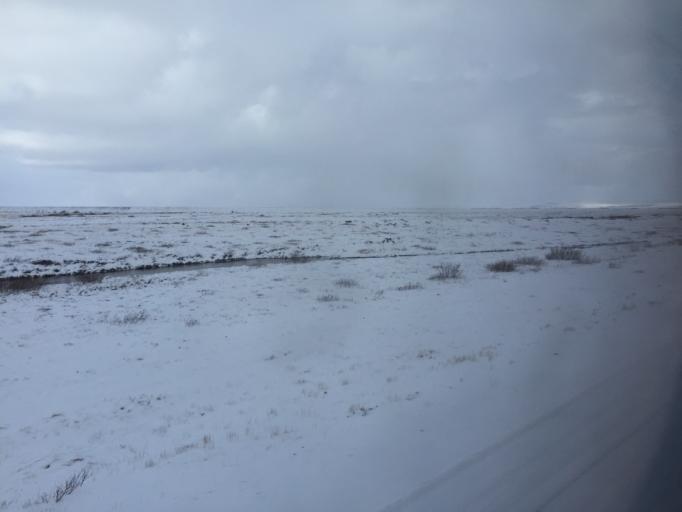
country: IS
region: South
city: Vestmannaeyjar
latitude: 63.6134
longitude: -19.9951
